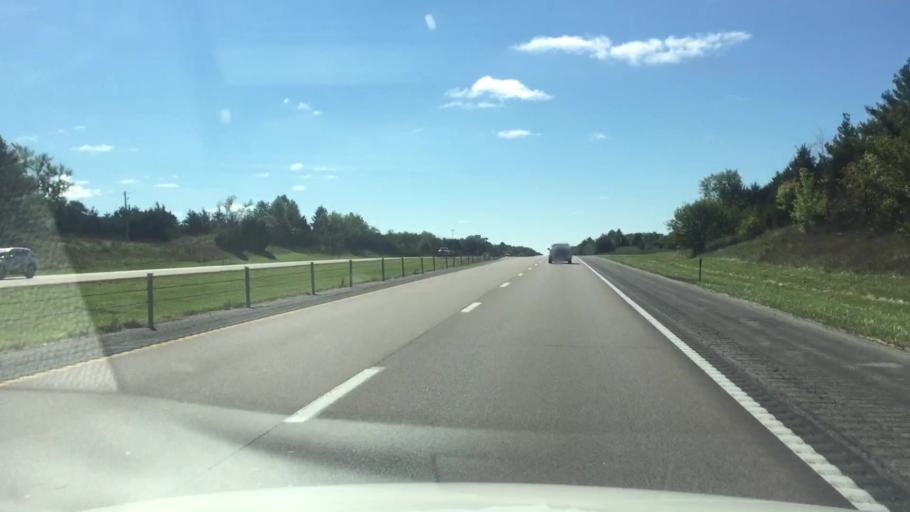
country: US
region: Missouri
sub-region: Boone County
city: Ashland
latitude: 38.7431
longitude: -92.2537
